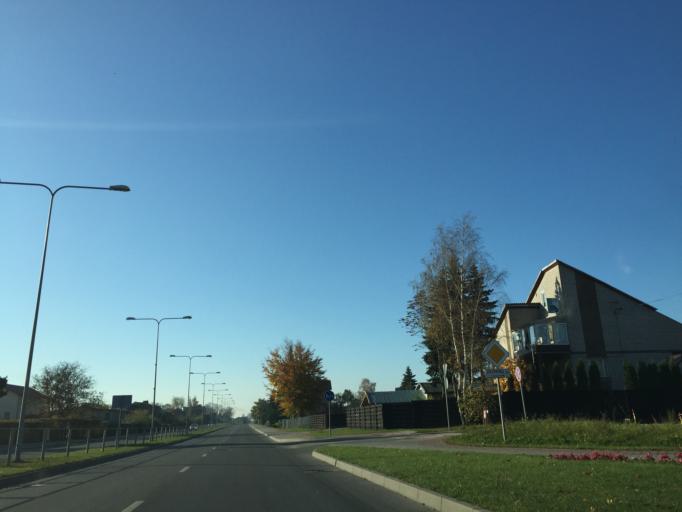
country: LT
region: Klaipedos apskritis
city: Kretinga
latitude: 55.8912
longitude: 21.2341
